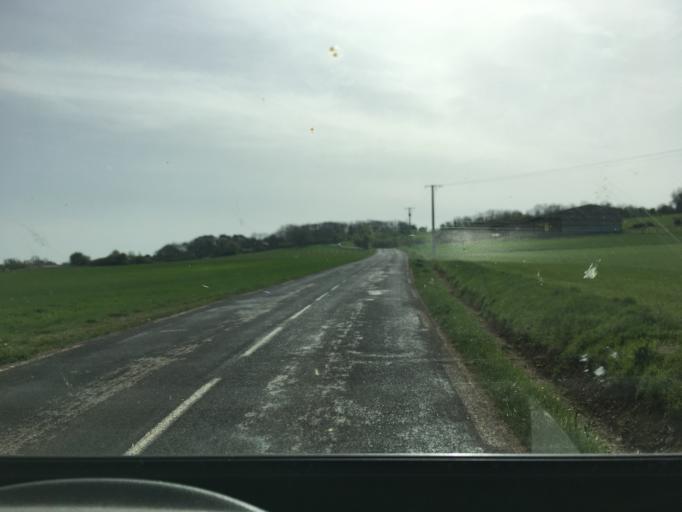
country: FR
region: Lorraine
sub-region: Departement de Meurthe-et-Moselle
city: Gondreville
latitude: 48.6620
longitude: 5.9665
